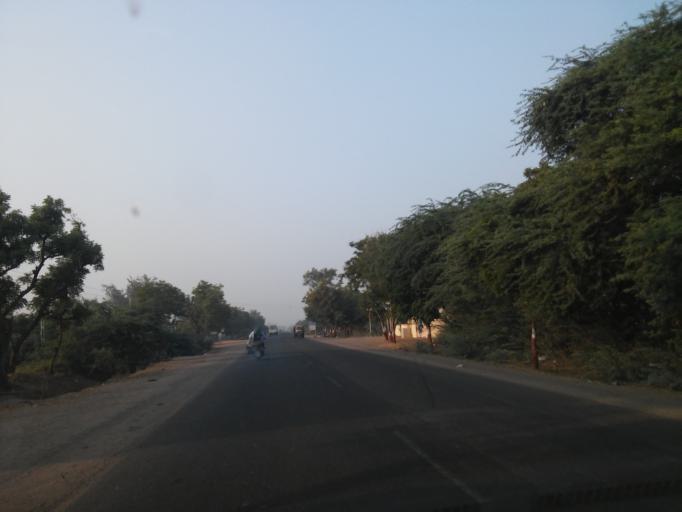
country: IN
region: Gujarat
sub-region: Kachchh
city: Mandvi
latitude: 22.8466
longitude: 69.3754
